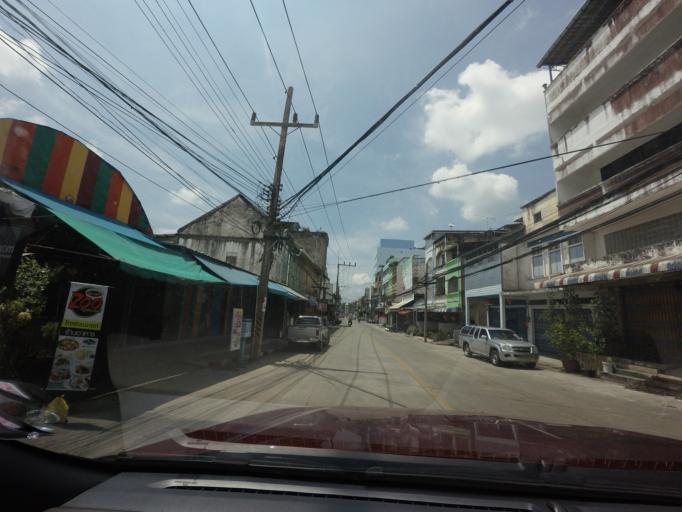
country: TH
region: Yala
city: Betong
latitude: 5.7716
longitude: 101.0688
